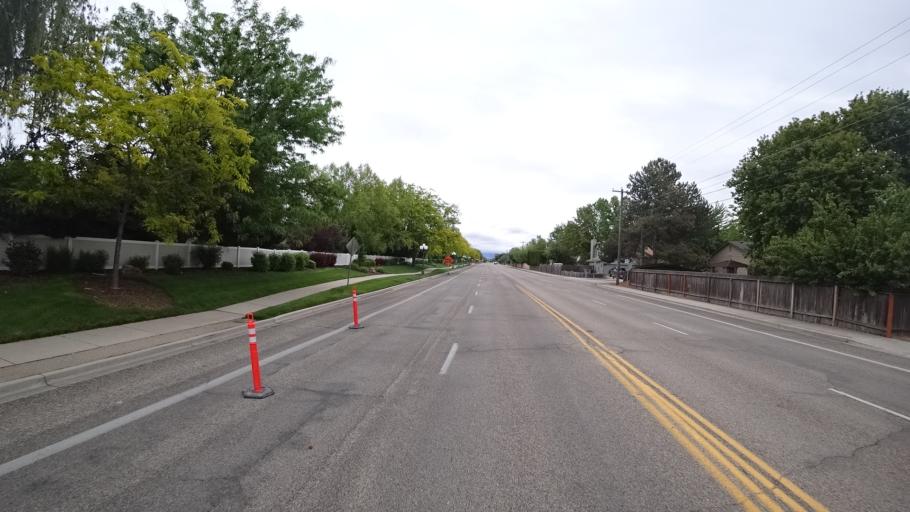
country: US
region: Idaho
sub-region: Ada County
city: Eagle
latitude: 43.6485
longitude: -116.3319
